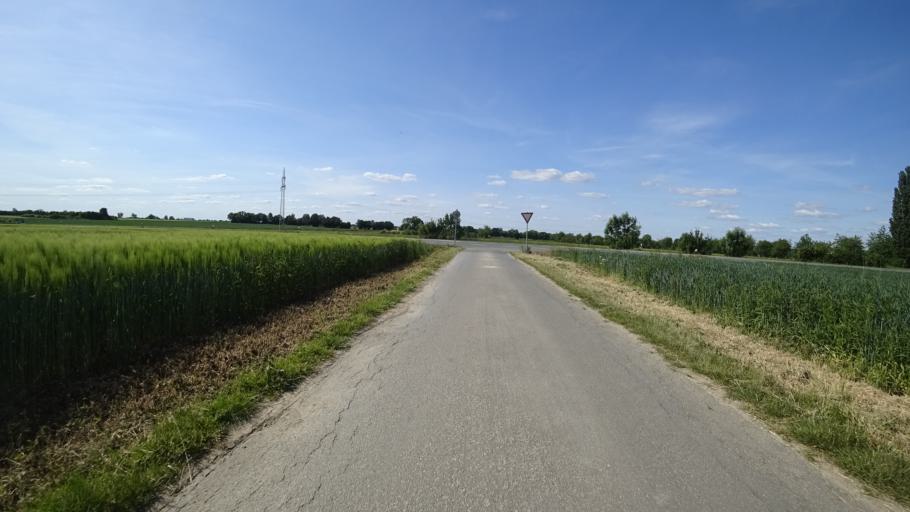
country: DE
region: North Rhine-Westphalia
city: Erwitte
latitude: 51.6177
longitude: 8.3698
